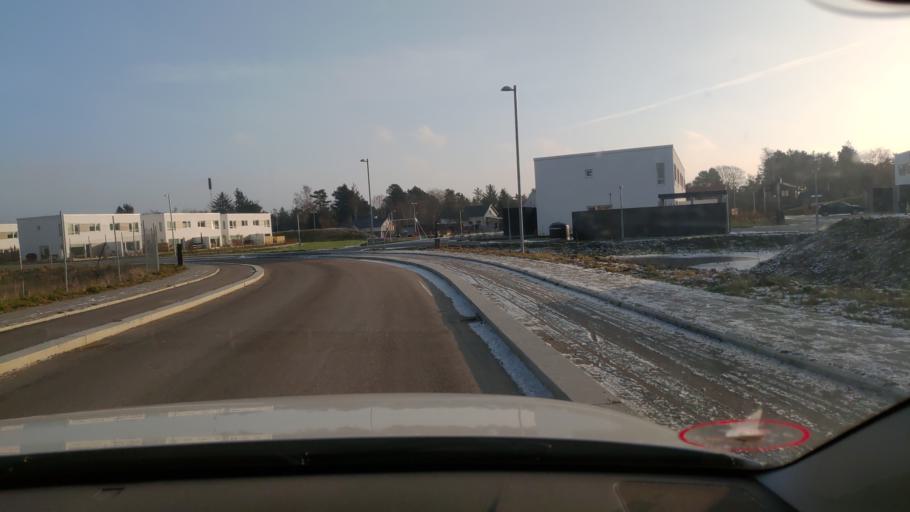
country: DK
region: Zealand
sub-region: Solrod Kommune
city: Solrod Strand
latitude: 55.5454
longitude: 12.2343
